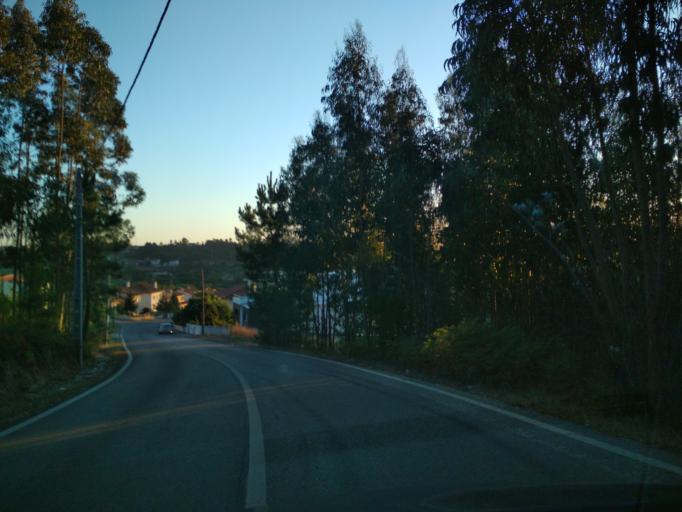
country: PT
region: Coimbra
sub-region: Condeixa-A-Nova
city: Condeixa-a-Nova
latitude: 40.1772
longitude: -8.4811
